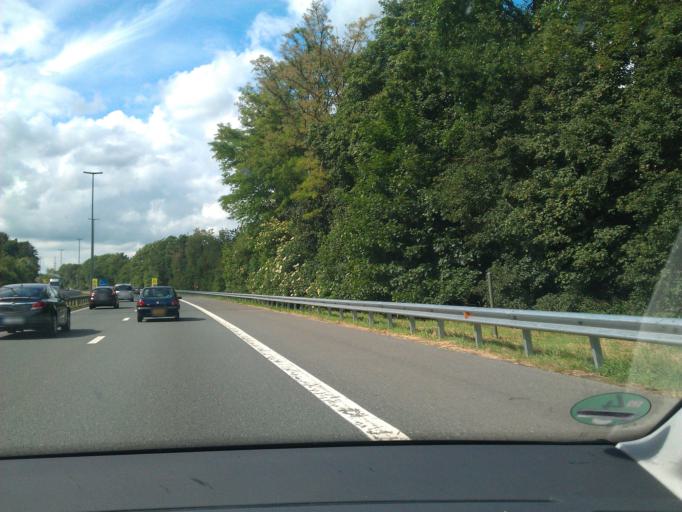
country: BE
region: Wallonia
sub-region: Province de Liege
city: Dison
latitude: 50.6188
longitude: 5.8538
